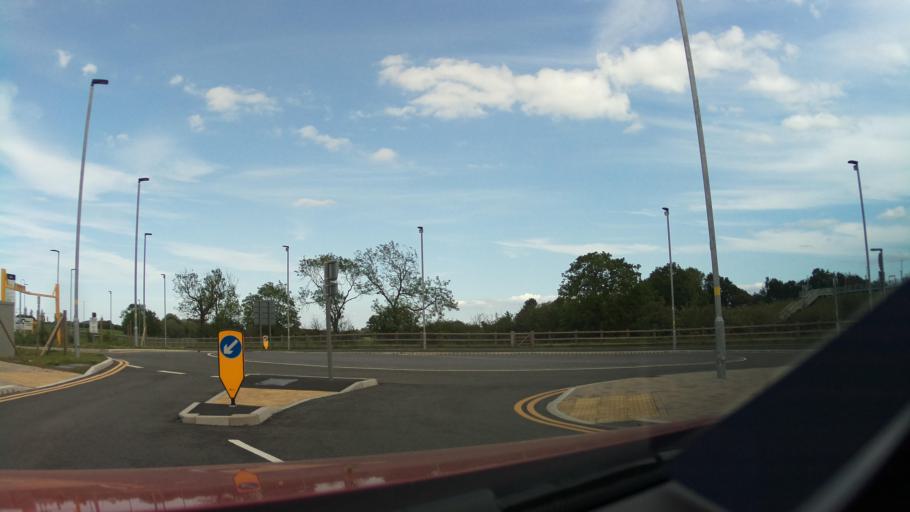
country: GB
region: England
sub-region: Worcestershire
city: Kempsey
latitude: 52.1569
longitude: -2.1585
